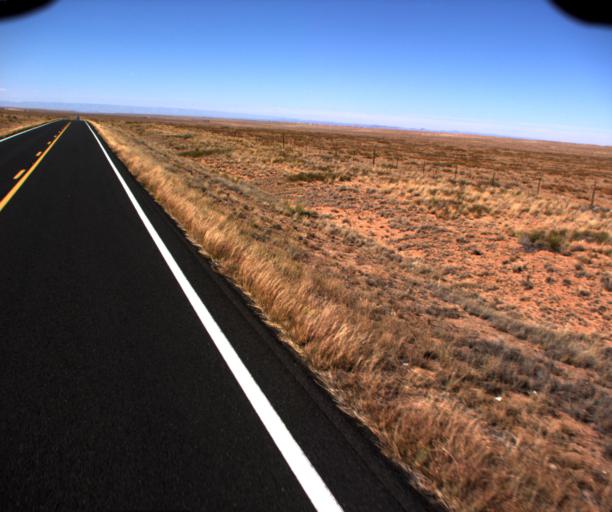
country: US
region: Arizona
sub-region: Coconino County
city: Tuba City
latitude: 36.0113
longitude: -111.0726
